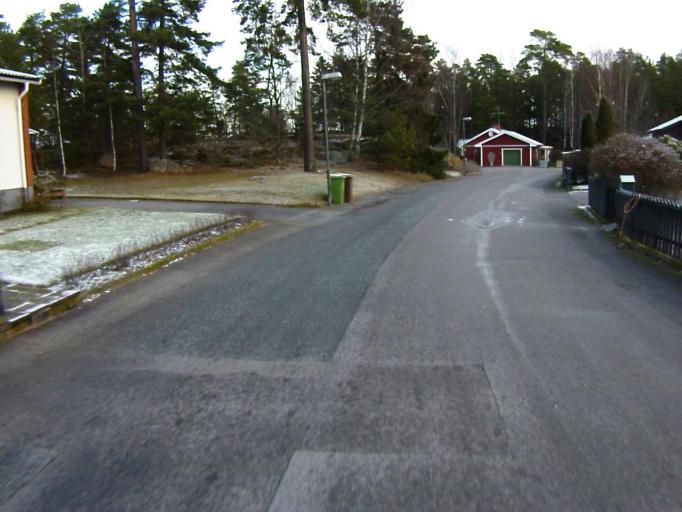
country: SE
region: Soedermanland
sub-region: Eskilstuna Kommun
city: Hallbybrunn
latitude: 59.3954
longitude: 16.4150
